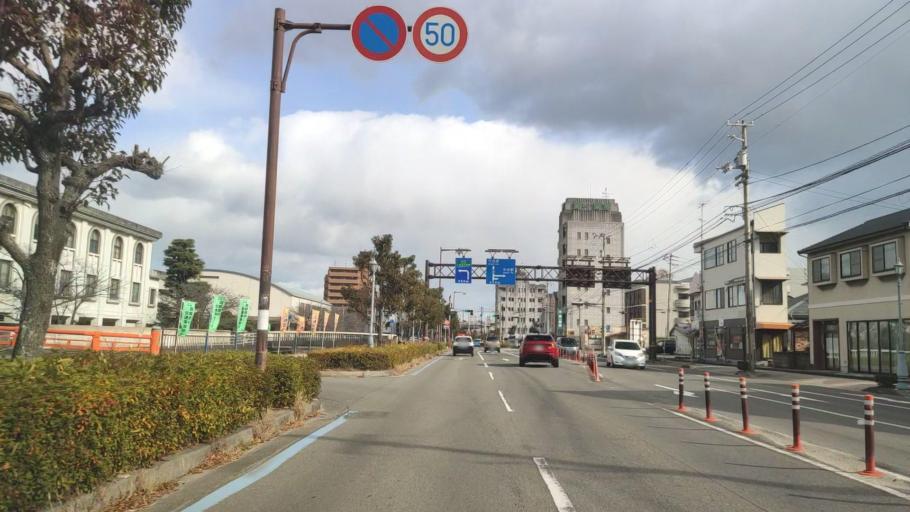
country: JP
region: Ehime
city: Hojo
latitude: 34.0642
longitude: 132.9885
